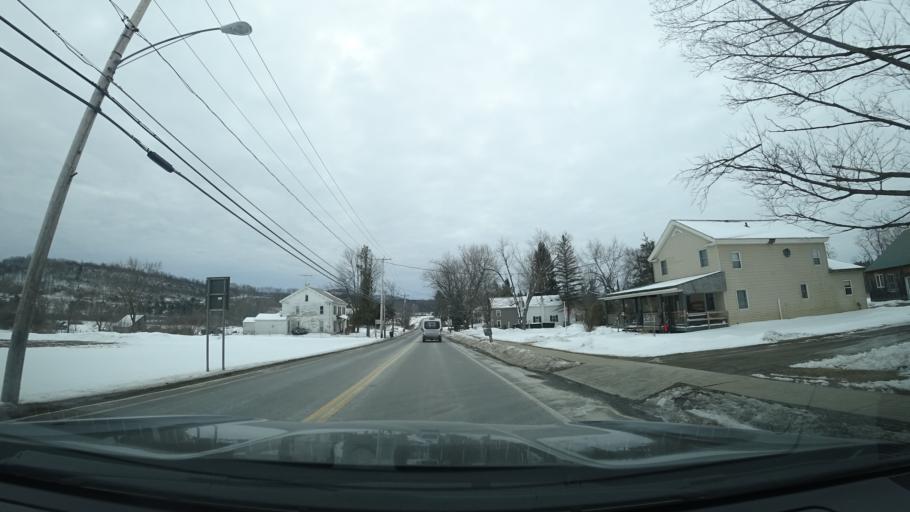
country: US
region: New York
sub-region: Washington County
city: Fort Edward
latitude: 43.2324
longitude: -73.4898
